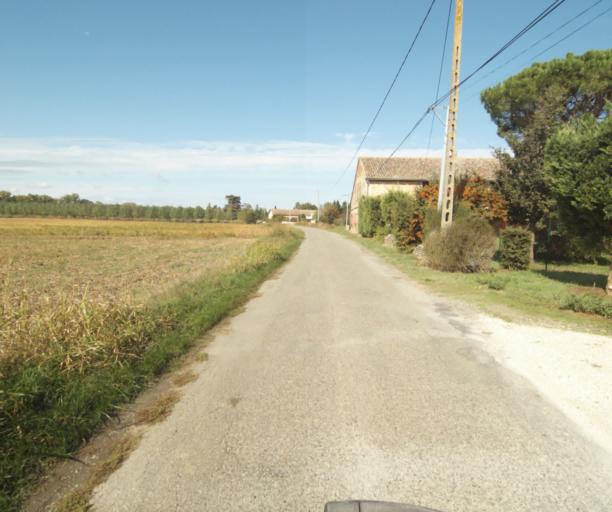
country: FR
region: Midi-Pyrenees
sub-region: Departement du Tarn-et-Garonne
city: Verdun-sur-Garonne
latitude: 43.8681
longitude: 1.2423
